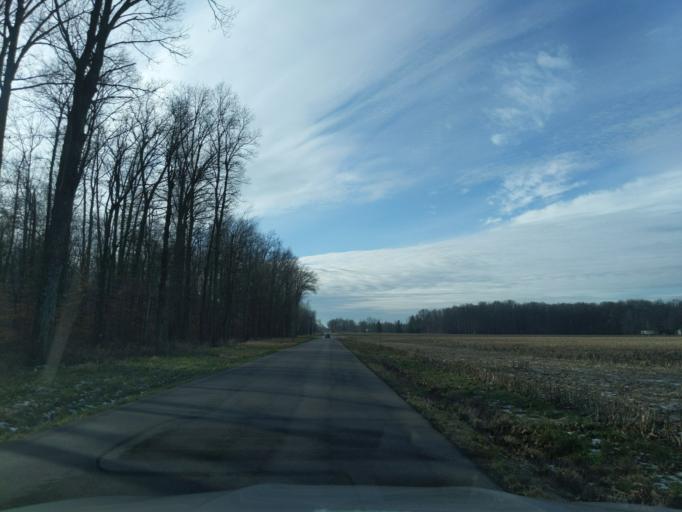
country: US
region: Indiana
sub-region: Decatur County
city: Westport
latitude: 39.1901
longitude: -85.4949
